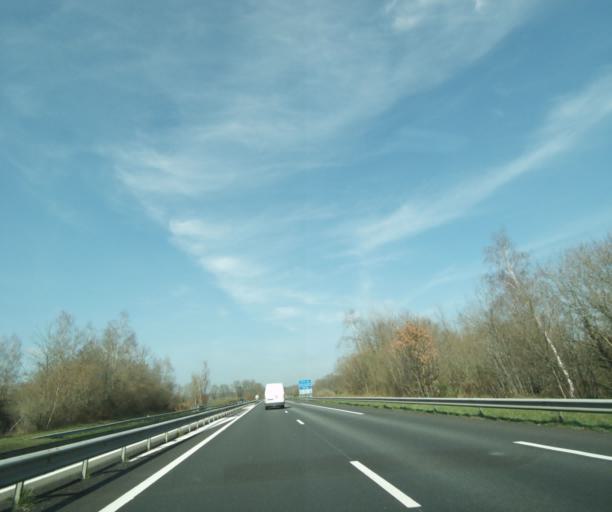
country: FR
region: Limousin
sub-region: Departement de la Haute-Vienne
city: Bessines-sur-Gartempe
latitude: 46.1683
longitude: 1.3769
